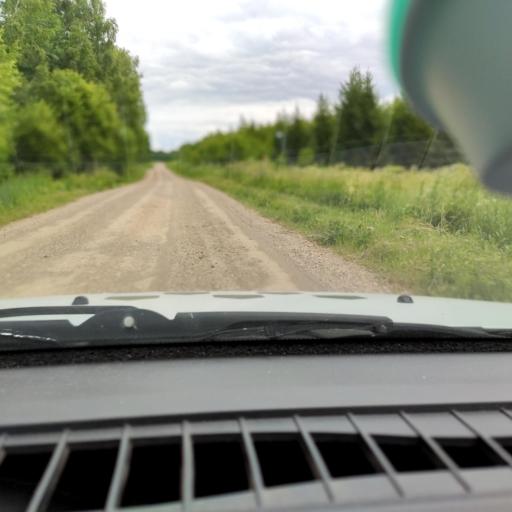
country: RU
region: Perm
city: Suksun
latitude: 57.2089
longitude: 57.6399
